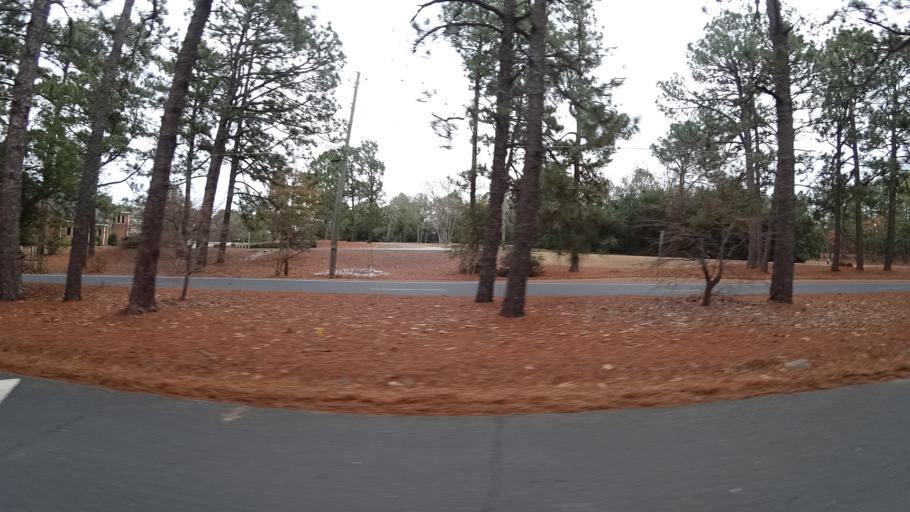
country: US
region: North Carolina
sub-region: Moore County
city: Southern Pines
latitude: 35.1809
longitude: -79.3815
